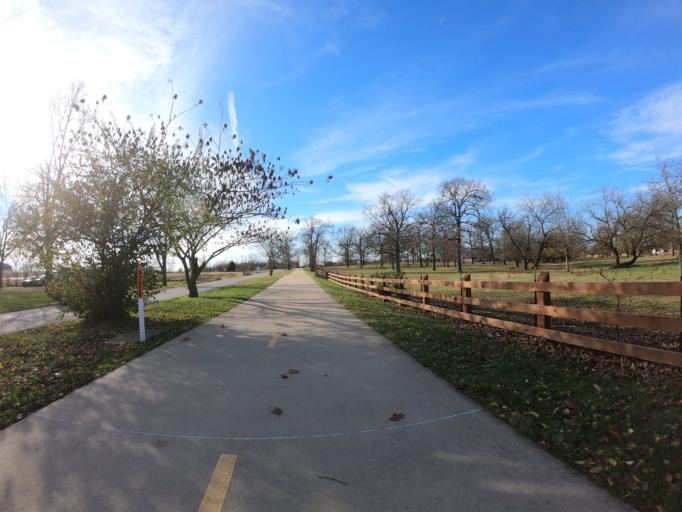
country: US
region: Arkansas
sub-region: Benton County
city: Lowell
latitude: 36.2657
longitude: -94.1608
